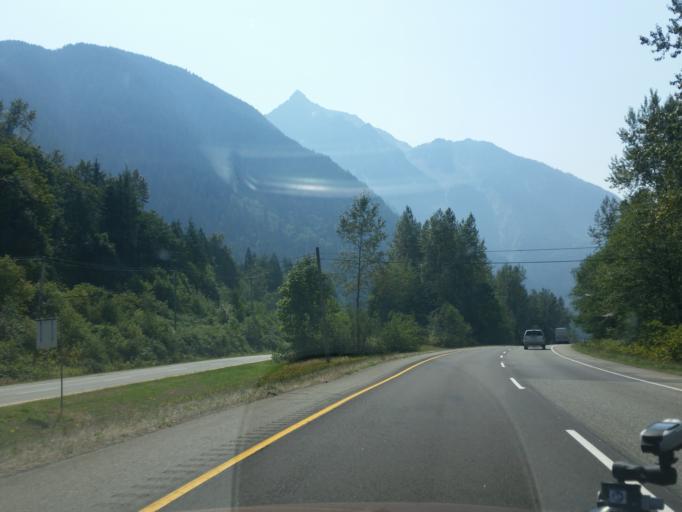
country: CA
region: British Columbia
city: Agassiz
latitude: 49.2345
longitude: -121.6818
